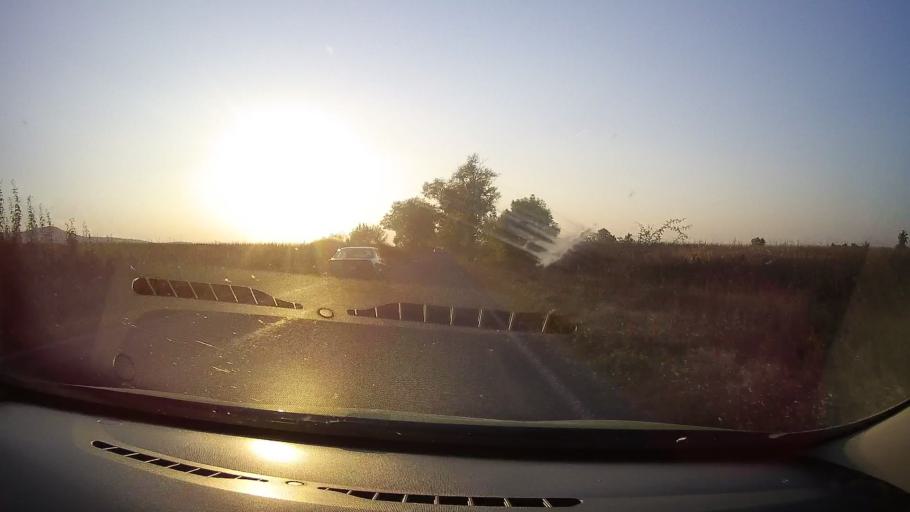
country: RO
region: Arad
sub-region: Comuna Bocsig
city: Bocsig
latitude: 46.4289
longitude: 21.8968
